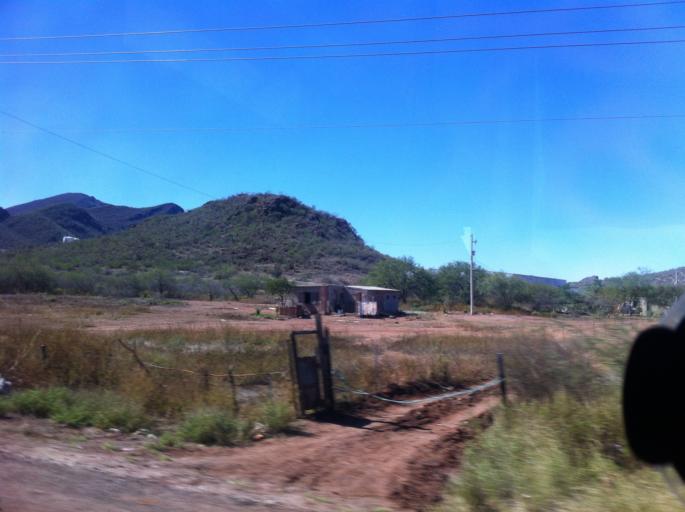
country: MX
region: Sonora
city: Heroica Guaymas
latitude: 27.9674
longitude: -110.9368
